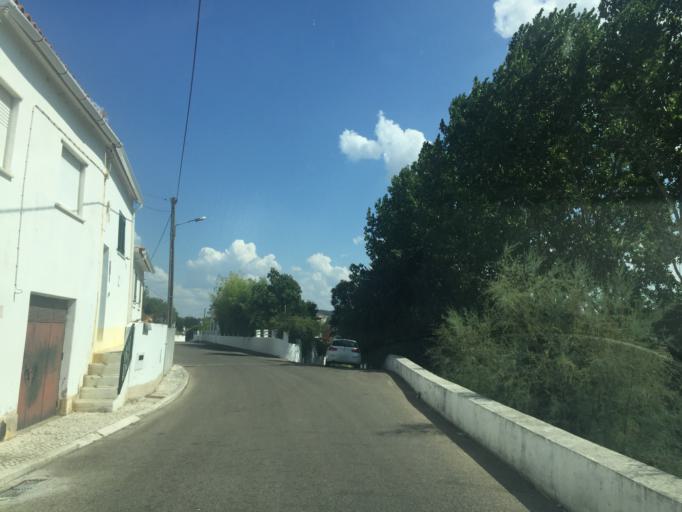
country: PT
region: Santarem
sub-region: Chamusca
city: Vila Nova da Barquinha
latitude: 39.4574
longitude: -8.4235
